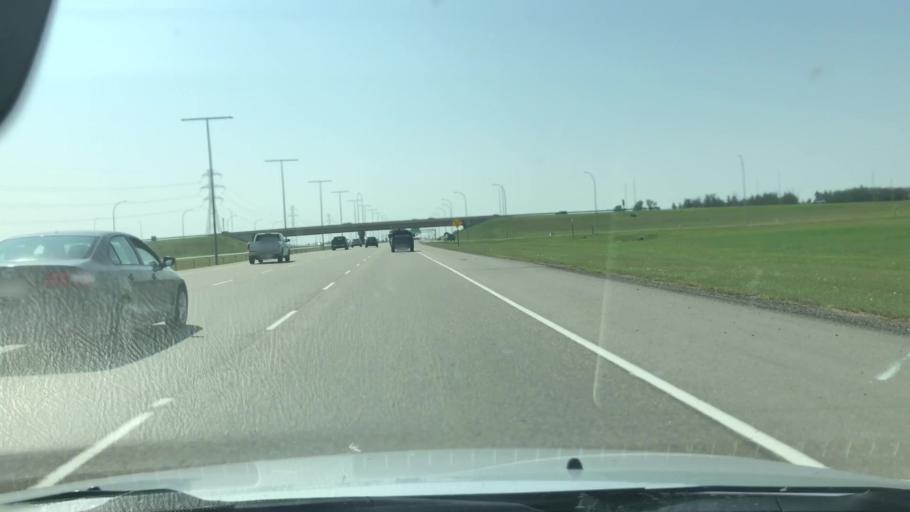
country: CA
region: Alberta
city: St. Albert
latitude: 53.5263
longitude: -113.6598
